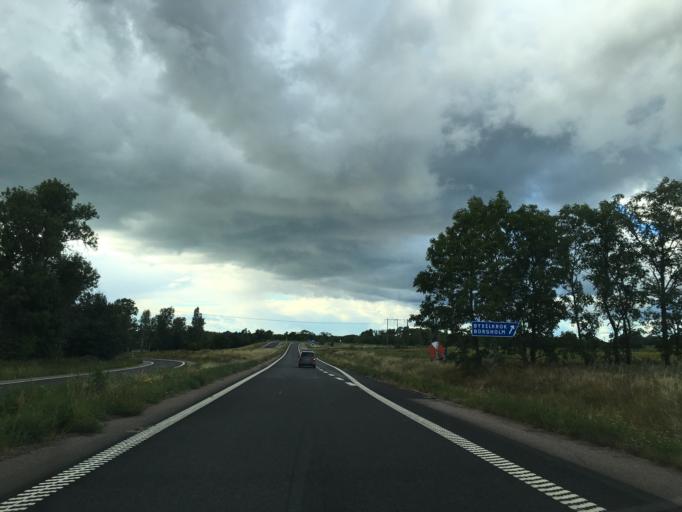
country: SE
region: Kalmar
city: Faerjestaden
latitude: 56.6689
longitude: 16.5174
